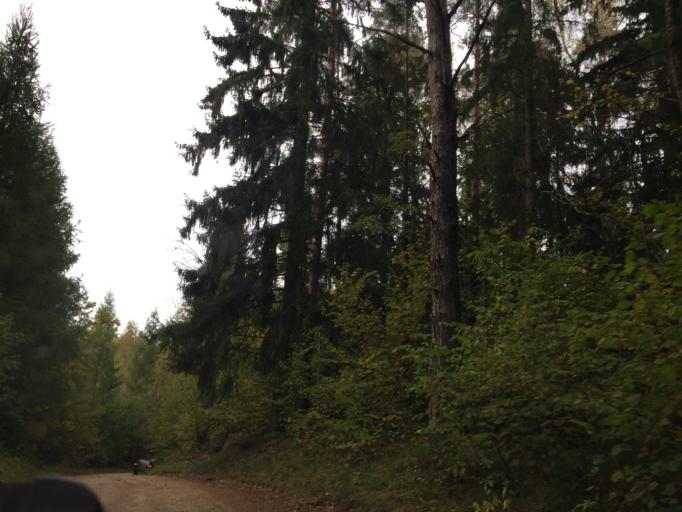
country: LV
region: Auces Novads
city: Auce
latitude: 56.5524
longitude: 23.0298
